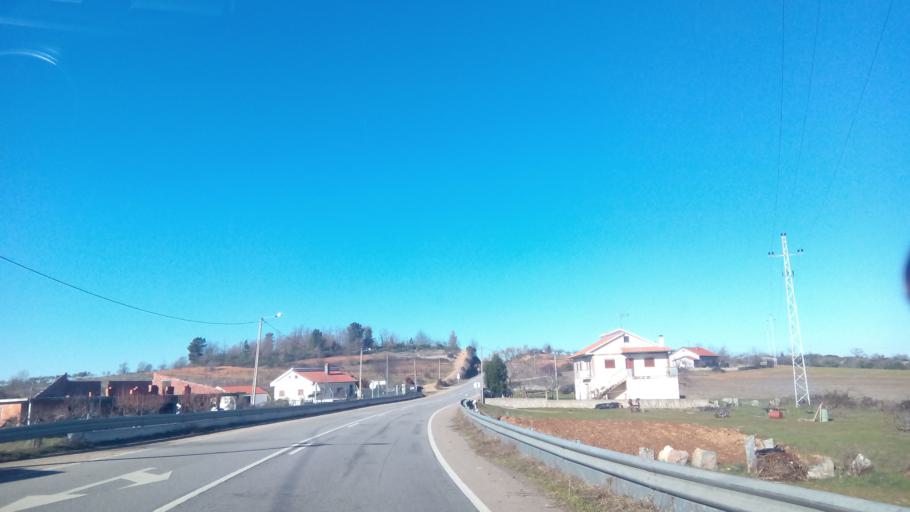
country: ES
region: Castille and Leon
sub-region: Provincia de Zamora
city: Trabazos
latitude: 41.7131
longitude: -6.6117
